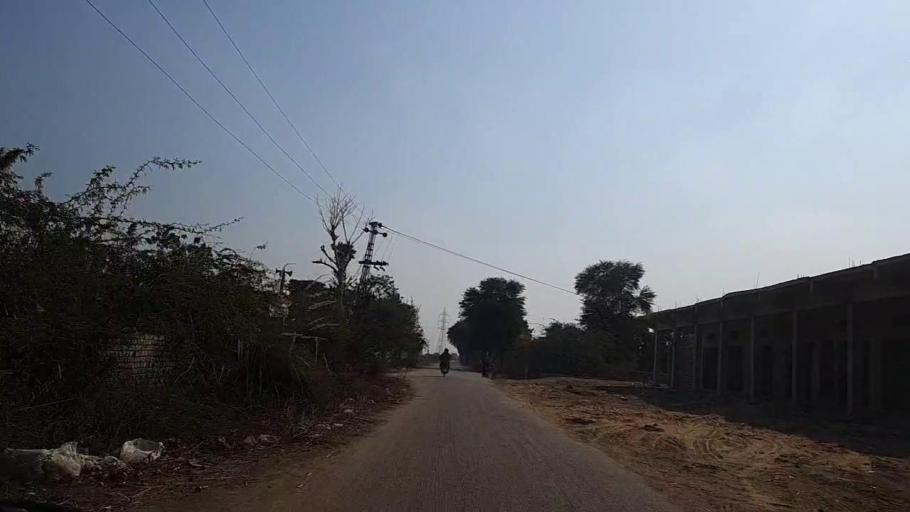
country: PK
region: Sindh
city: Sakrand
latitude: 26.1109
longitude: 68.2909
